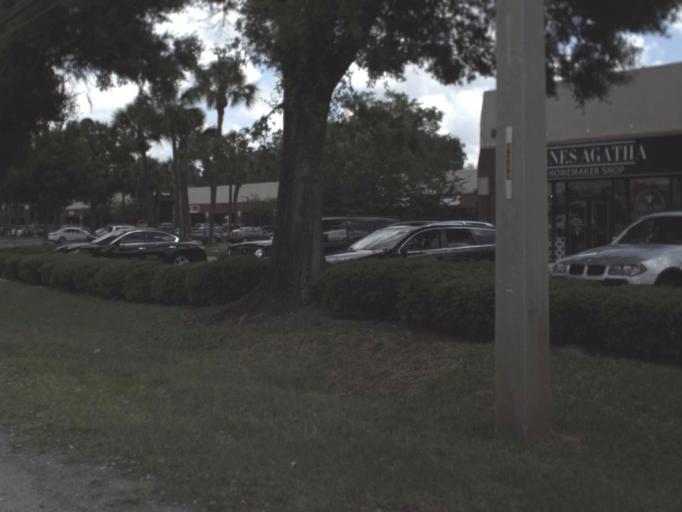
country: US
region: Florida
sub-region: Saint Johns County
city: Fruit Cove
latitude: 30.2219
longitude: -81.5862
